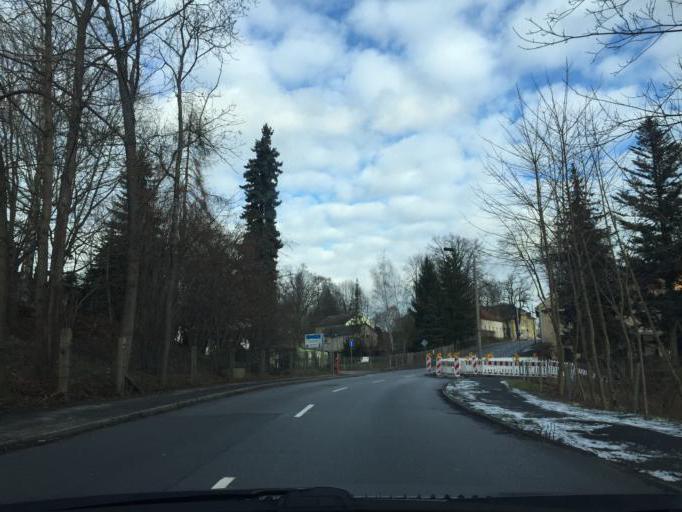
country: DE
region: Saxony
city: Radeberg
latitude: 51.1220
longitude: 13.9263
